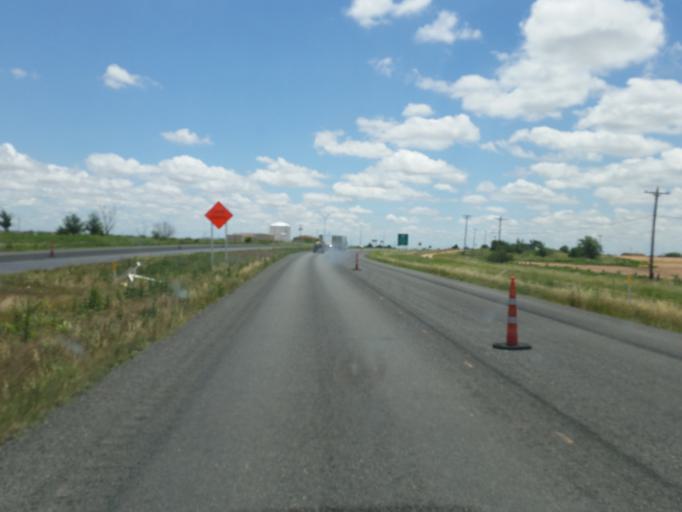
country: US
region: Texas
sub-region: Scurry County
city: Snyder
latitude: 32.7110
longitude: -100.8731
